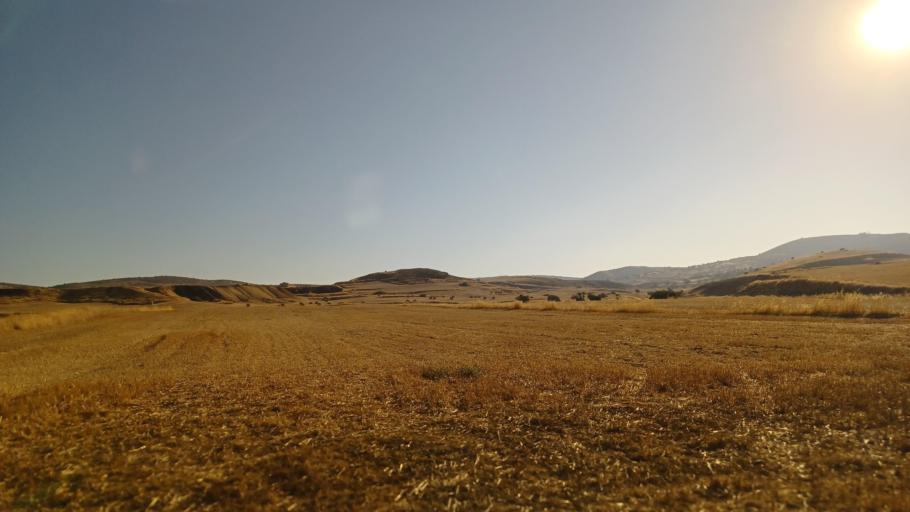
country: CY
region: Larnaka
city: Troulloi
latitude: 35.0233
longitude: 33.6383
